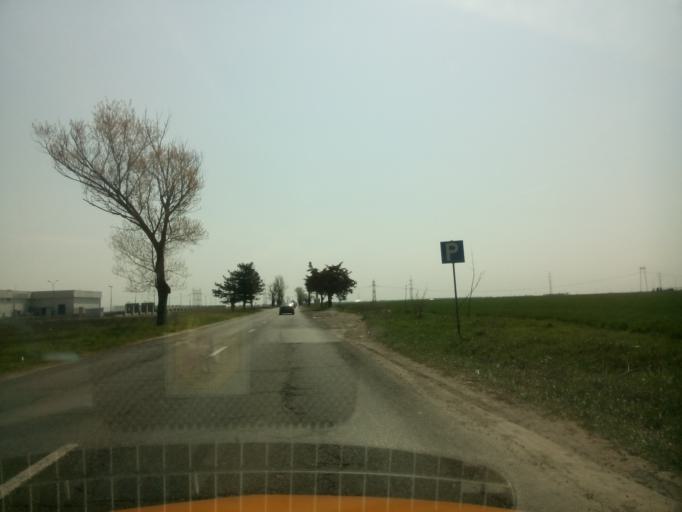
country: RO
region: Ilfov
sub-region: Comuna Berceni
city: Berceni
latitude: 44.3539
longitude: 26.2107
